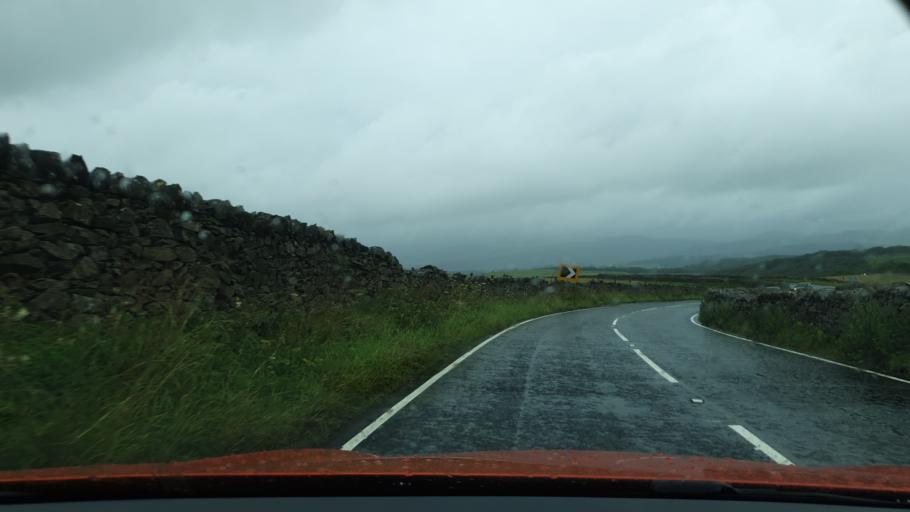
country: GB
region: England
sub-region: Cumbria
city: Ulverston
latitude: 54.2553
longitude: -3.1413
